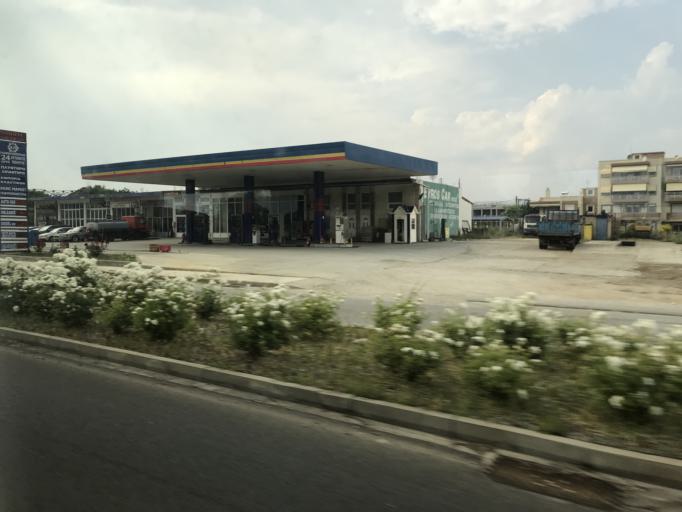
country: GR
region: East Macedonia and Thrace
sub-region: Nomos Evrou
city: Alexandroupoli
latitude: 40.8495
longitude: 25.8981
